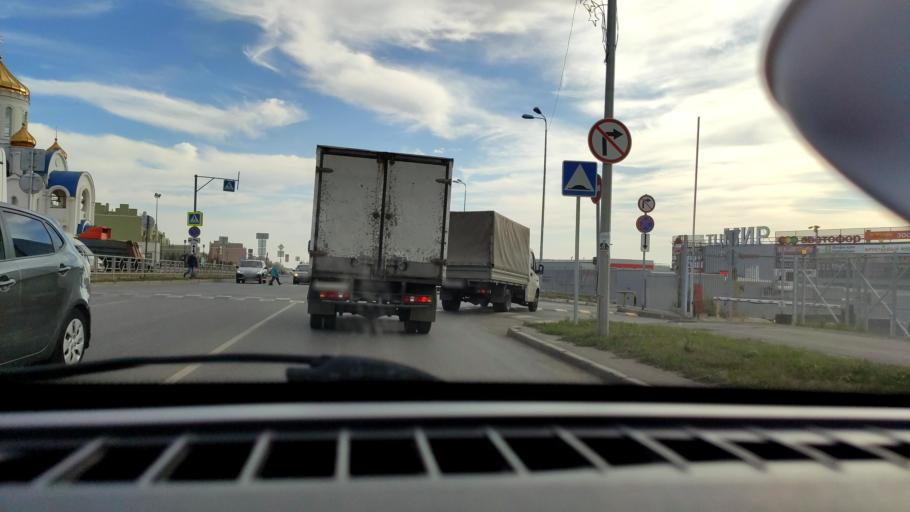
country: RU
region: Samara
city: Petra-Dubrava
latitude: 53.3172
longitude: 50.3034
